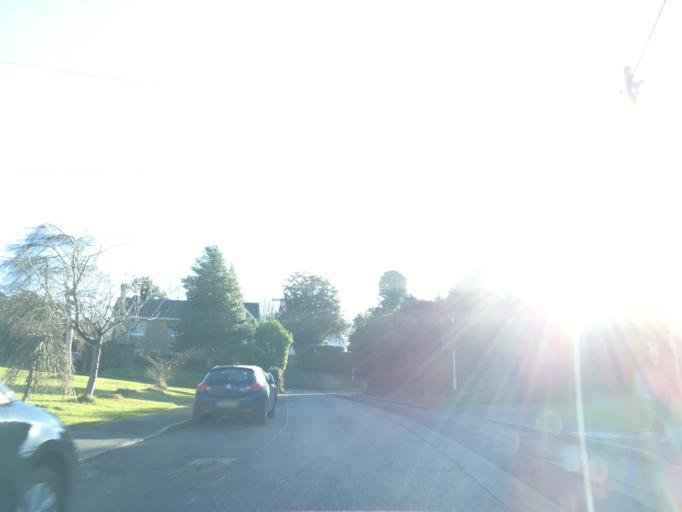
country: GB
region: England
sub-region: Borough of Swindon
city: Wroughton
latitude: 51.5232
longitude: -1.7865
